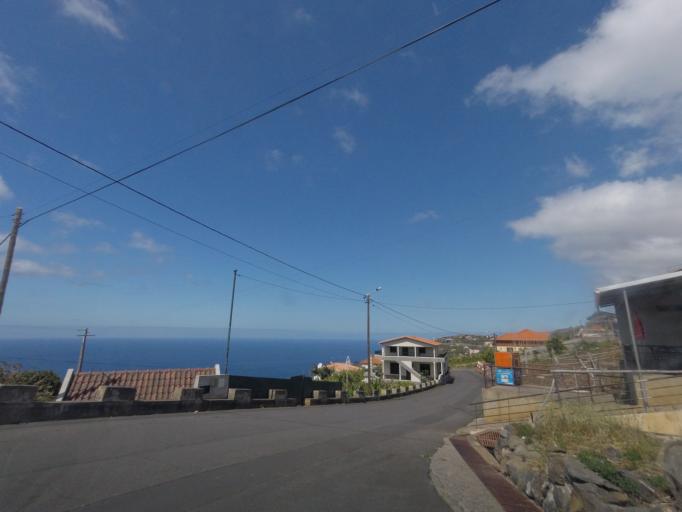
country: PT
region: Madeira
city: Ponta do Sol
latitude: 32.6840
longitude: -17.0792
